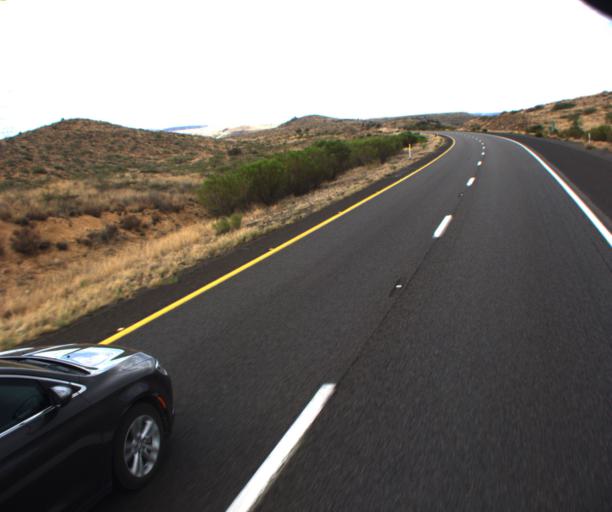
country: US
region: Arizona
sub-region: Yavapai County
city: Cordes Lakes
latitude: 34.2645
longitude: -112.1168
